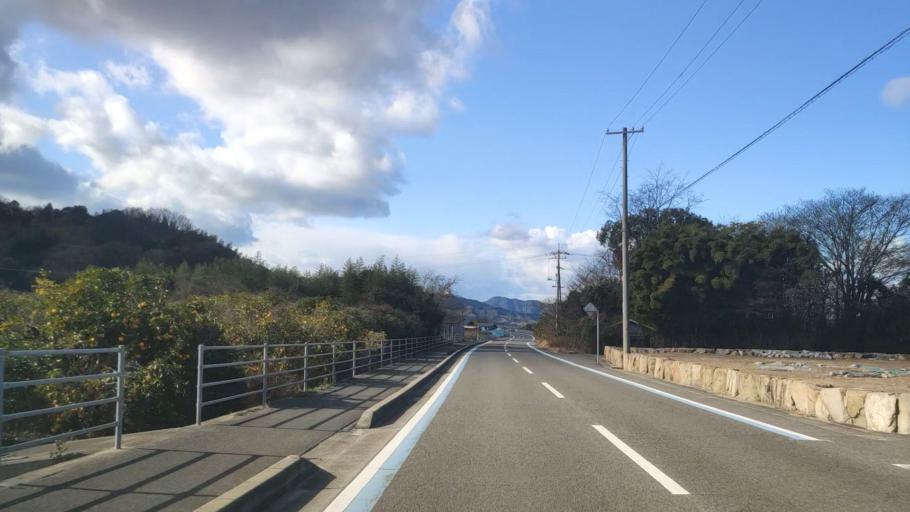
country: JP
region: Hiroshima
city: Innoshima
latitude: 34.2305
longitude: 133.0891
